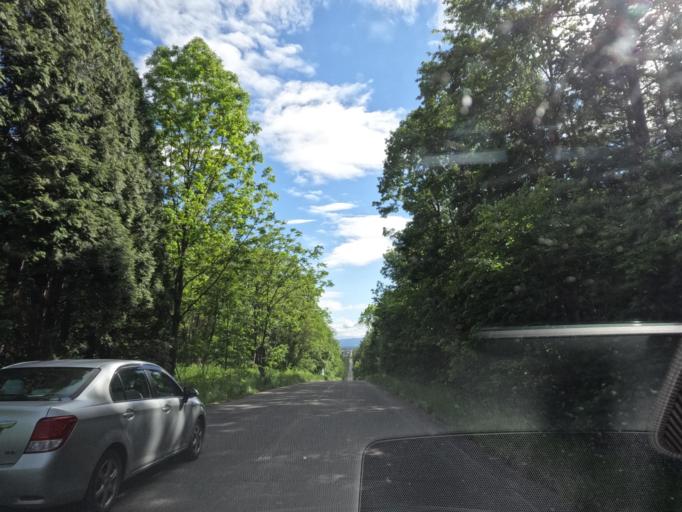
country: JP
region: Hokkaido
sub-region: Asahikawa-shi
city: Asahikawa
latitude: 43.7344
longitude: 142.5376
